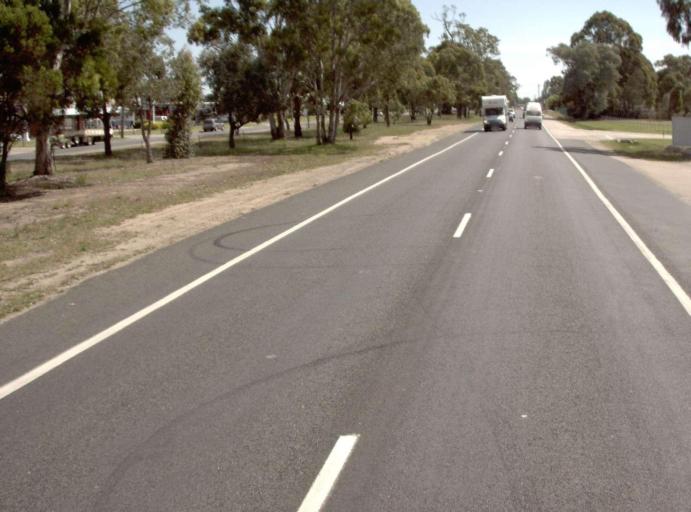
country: AU
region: Victoria
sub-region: East Gippsland
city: Bairnsdale
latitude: -37.8351
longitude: 147.6023
